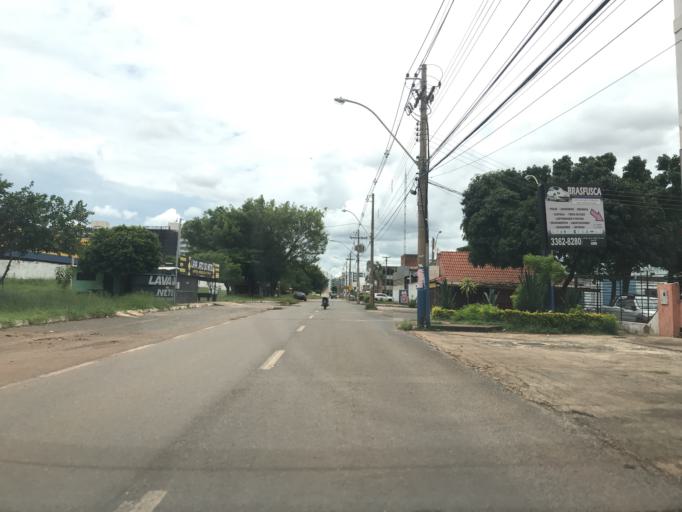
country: BR
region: Federal District
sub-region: Brasilia
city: Brasilia
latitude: -15.8238
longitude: -47.9565
